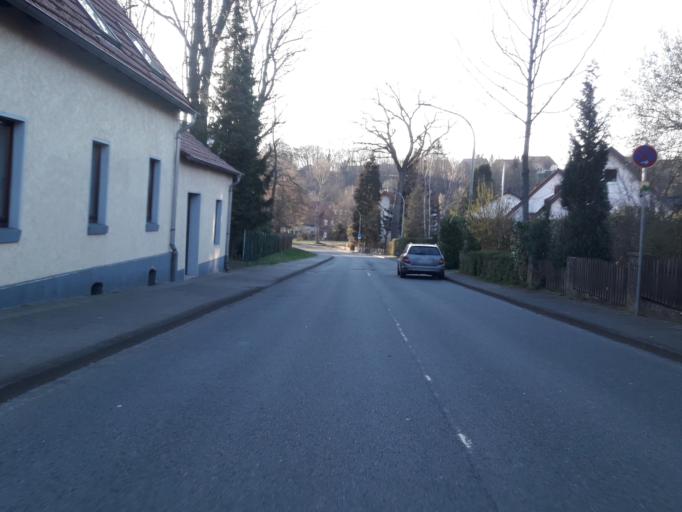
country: DE
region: North Rhine-Westphalia
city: Bad Lippspringe
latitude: 51.7465
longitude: 8.8563
